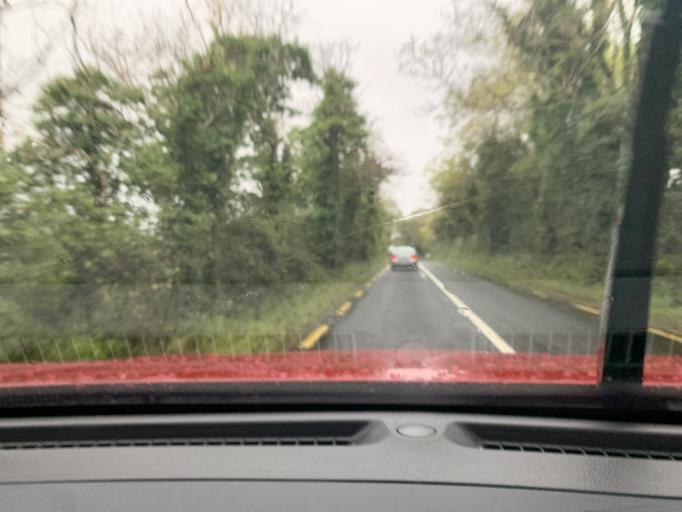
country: IE
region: Connaught
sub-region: Sligo
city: Sligo
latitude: 54.3331
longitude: -8.3916
